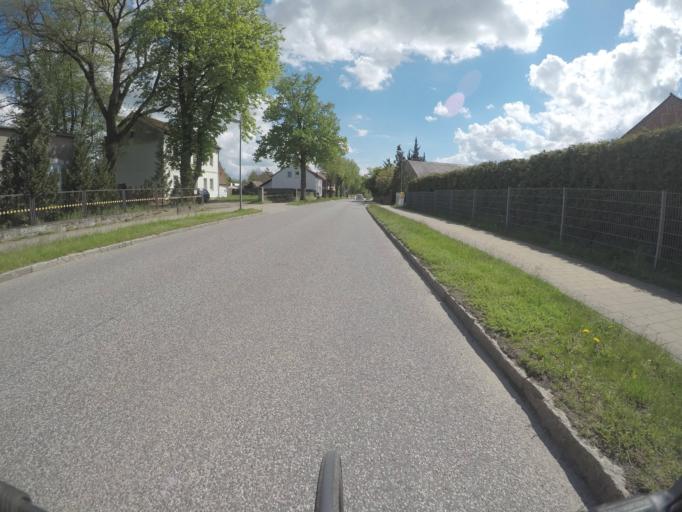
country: DE
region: Brandenburg
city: Bernau bei Berlin
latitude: 52.7005
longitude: 13.5881
